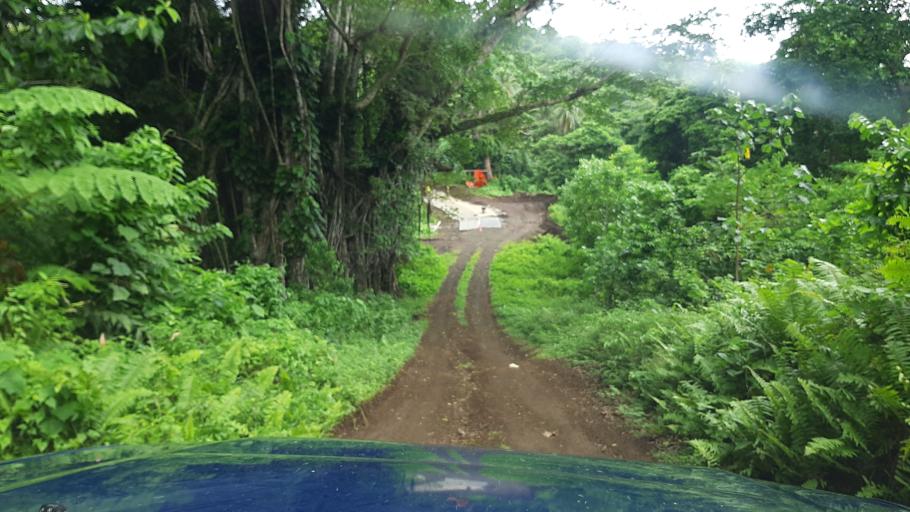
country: VU
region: Shefa
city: Port-Vila
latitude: -16.9012
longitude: 168.5721
